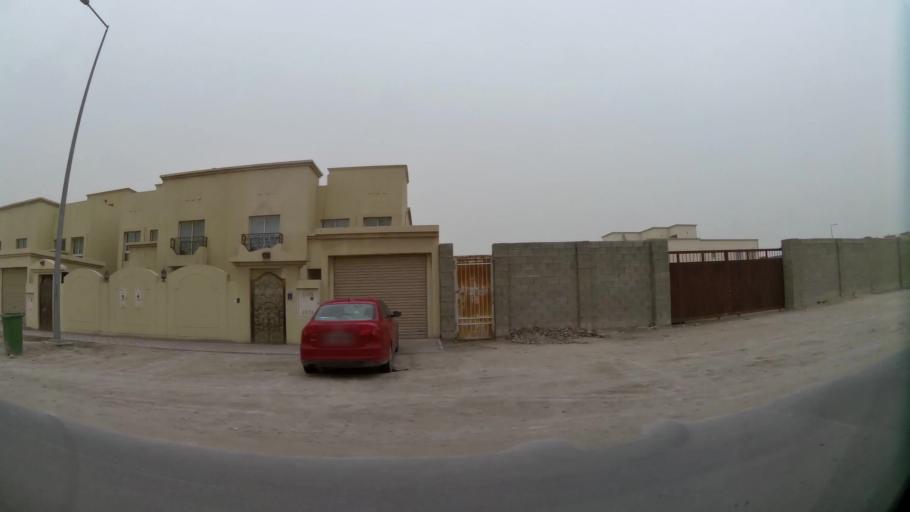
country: QA
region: Baladiyat ad Dawhah
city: Doha
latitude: 25.2440
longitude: 51.4875
